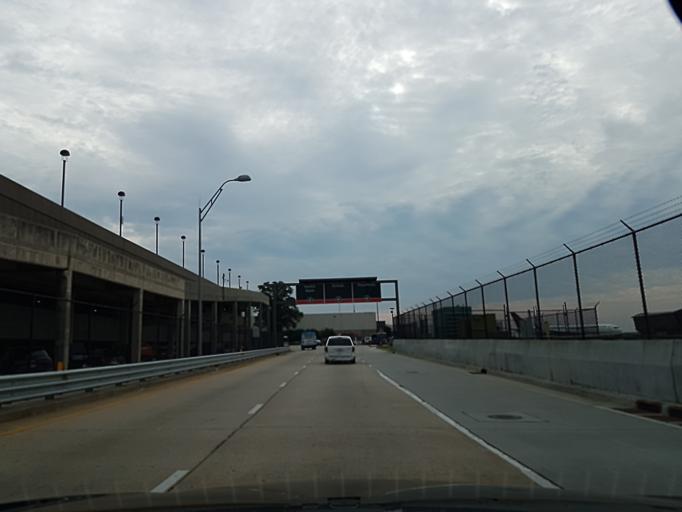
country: US
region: Georgia
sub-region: Fulton County
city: College Park
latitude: 33.6374
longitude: -84.4445
